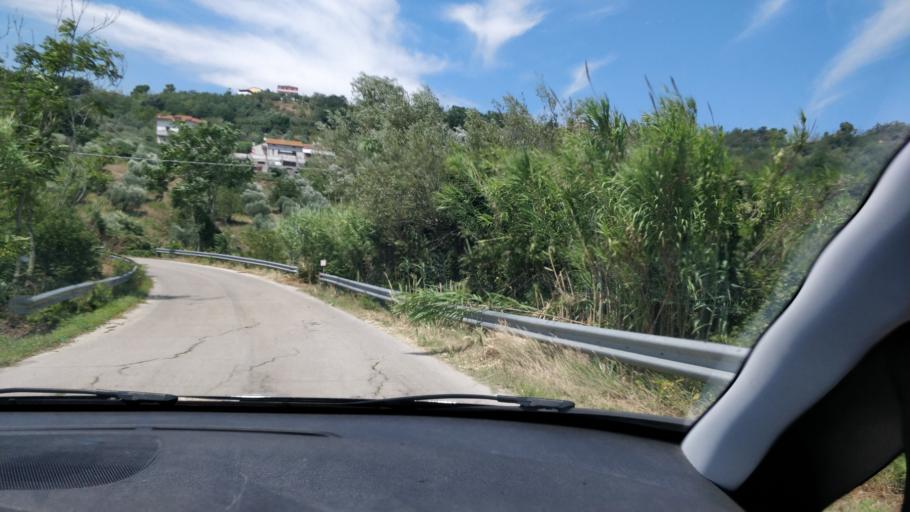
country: IT
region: Abruzzo
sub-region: Provincia di Chieti
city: Sambuceto
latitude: 42.4121
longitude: 14.2091
